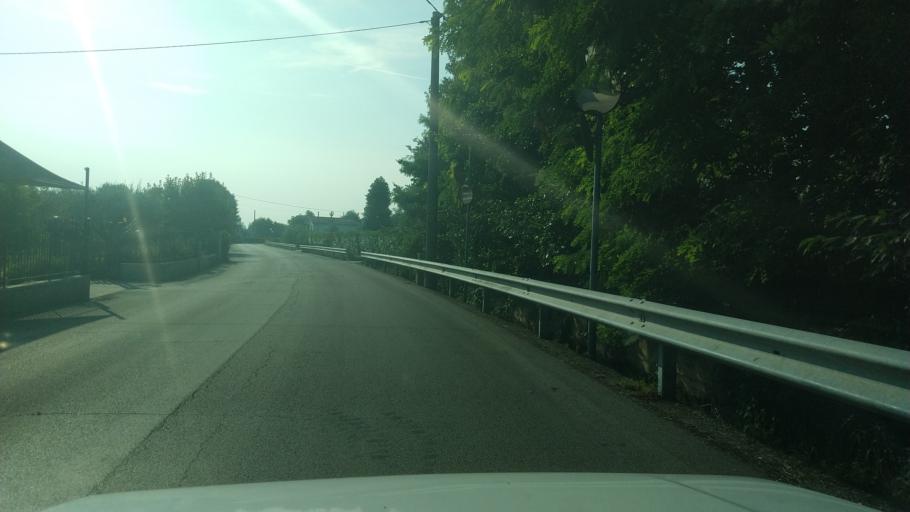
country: IT
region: Veneto
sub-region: Provincia di Vicenza
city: Mason Vicentino
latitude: 45.7229
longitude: 11.6185
